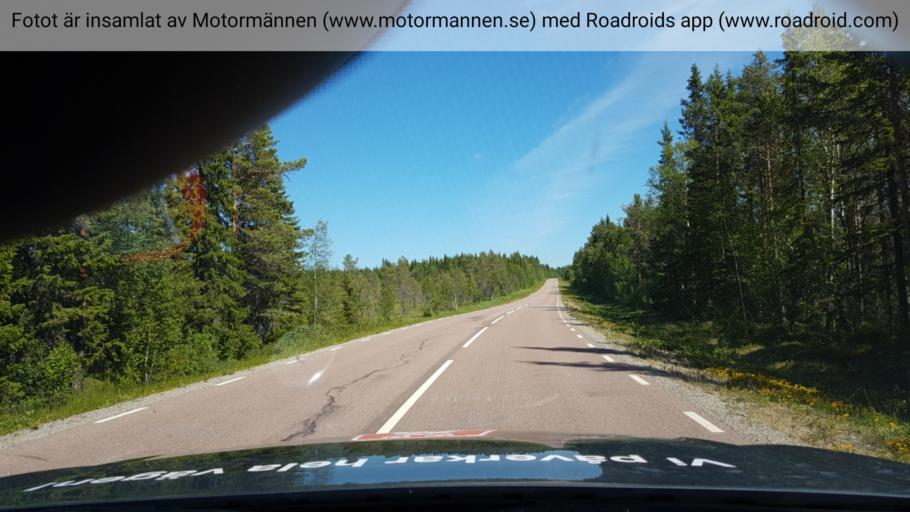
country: SE
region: Jaemtland
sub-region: Braecke Kommun
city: Braecke
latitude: 62.7512
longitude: 15.2514
